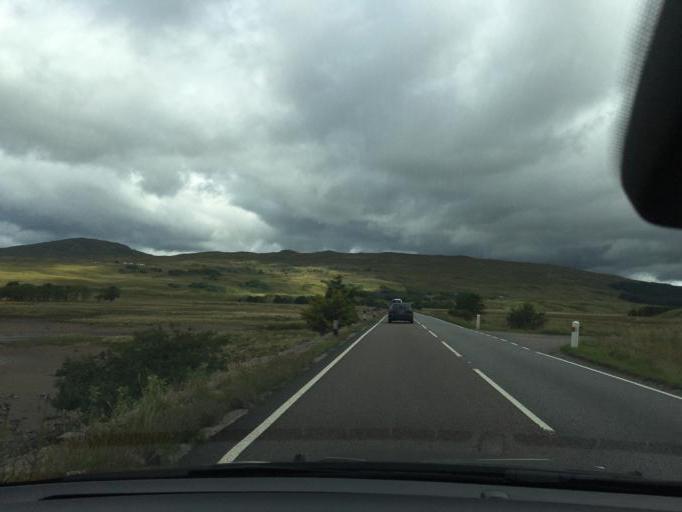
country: GB
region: Scotland
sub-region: Highland
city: Spean Bridge
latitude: 56.5542
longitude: -4.7492
